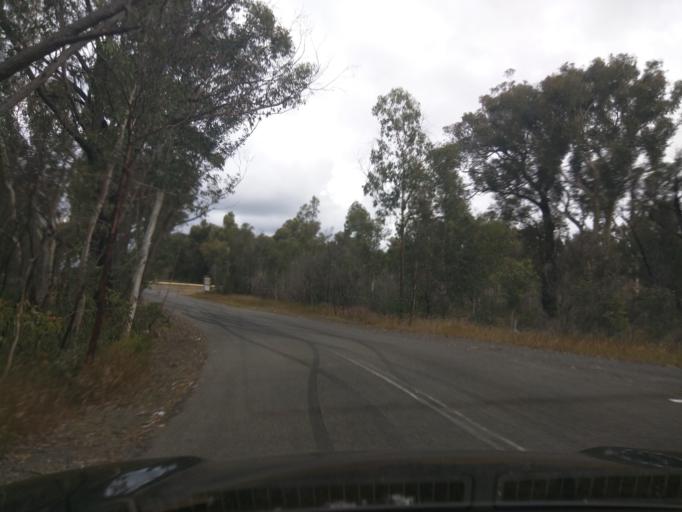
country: AU
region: New South Wales
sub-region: Wollondilly
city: Douglas Park
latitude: -34.3091
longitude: 150.7386
